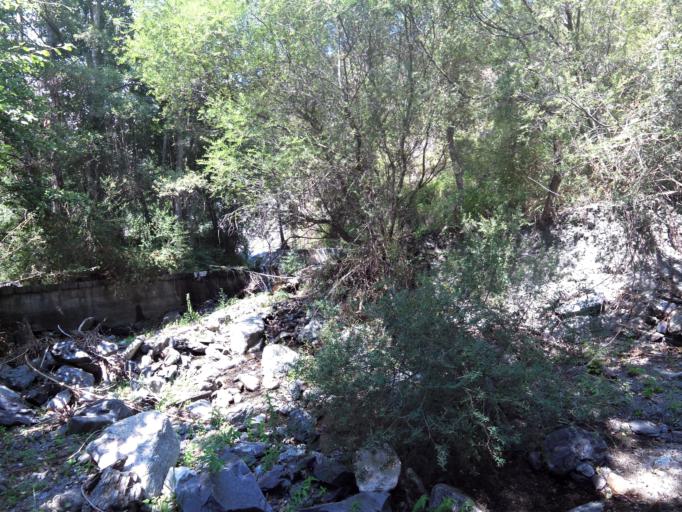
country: IT
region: Calabria
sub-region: Provincia di Reggio Calabria
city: Pazzano
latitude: 38.4742
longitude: 16.4347
